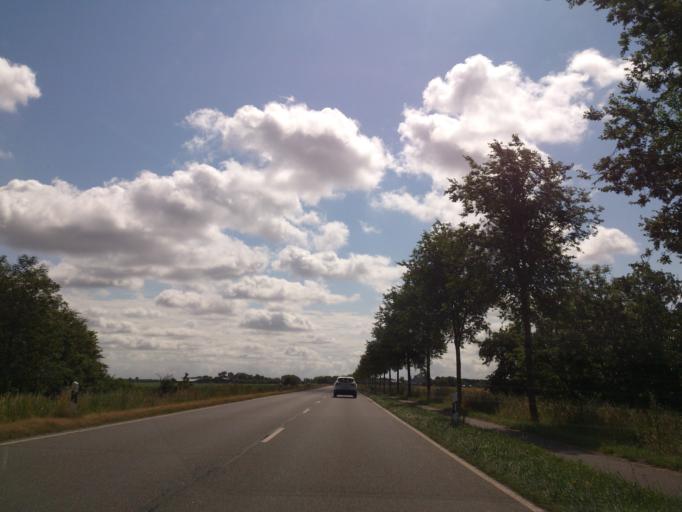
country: DE
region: Schleswig-Holstein
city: Grothusenkoog
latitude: 54.3024
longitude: 8.7669
